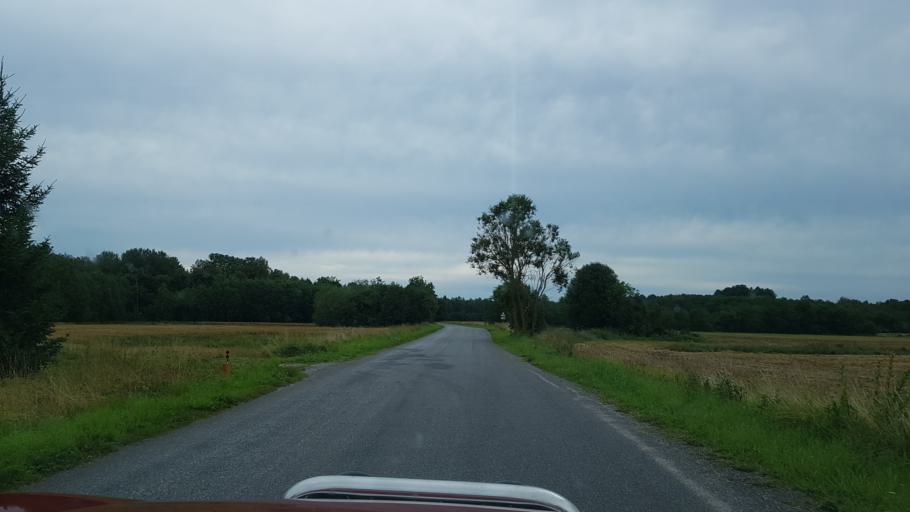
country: EE
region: Laeaene
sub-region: Lihula vald
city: Lihula
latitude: 58.8381
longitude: 23.8137
